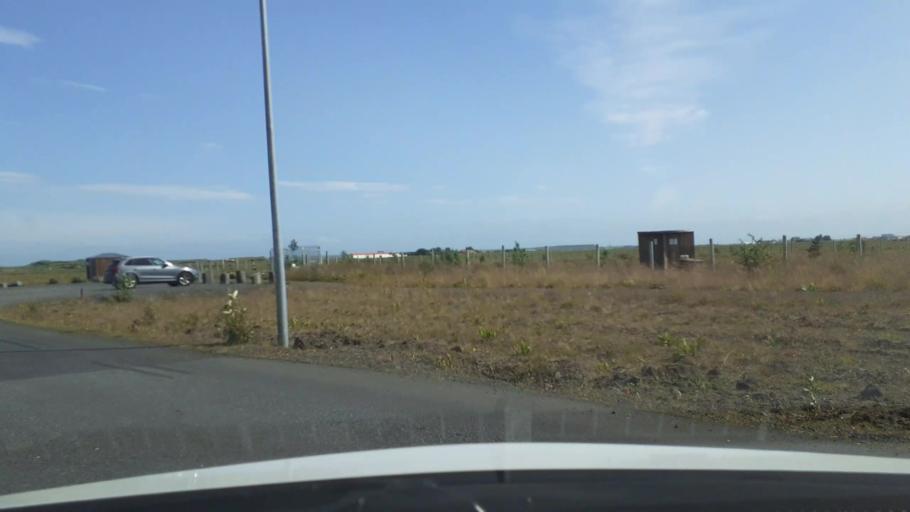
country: IS
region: South
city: Selfoss
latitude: 63.9243
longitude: -20.9826
